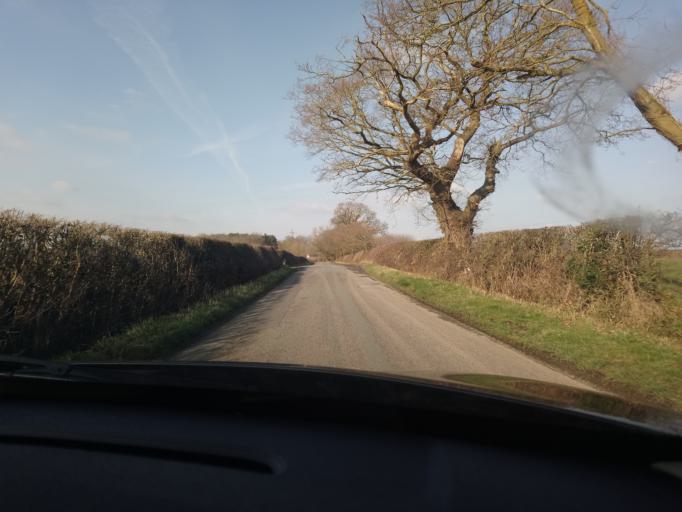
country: GB
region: England
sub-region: Shropshire
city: Bicton
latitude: 52.7583
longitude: -2.7774
